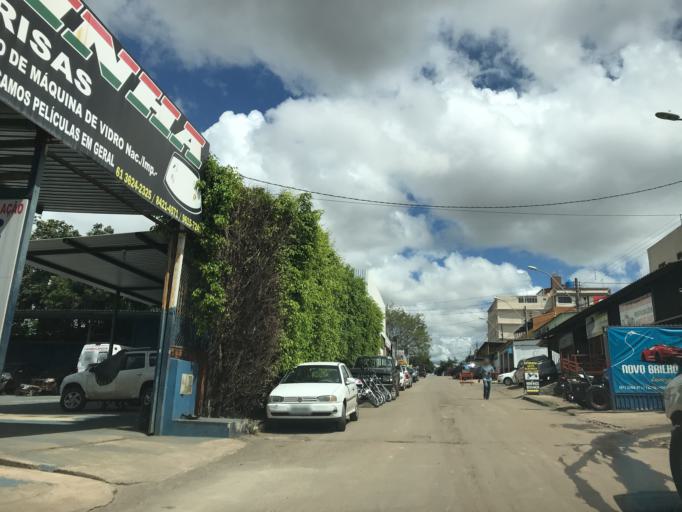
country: BR
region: Federal District
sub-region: Brasilia
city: Brasilia
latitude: -15.8361
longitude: -47.9874
